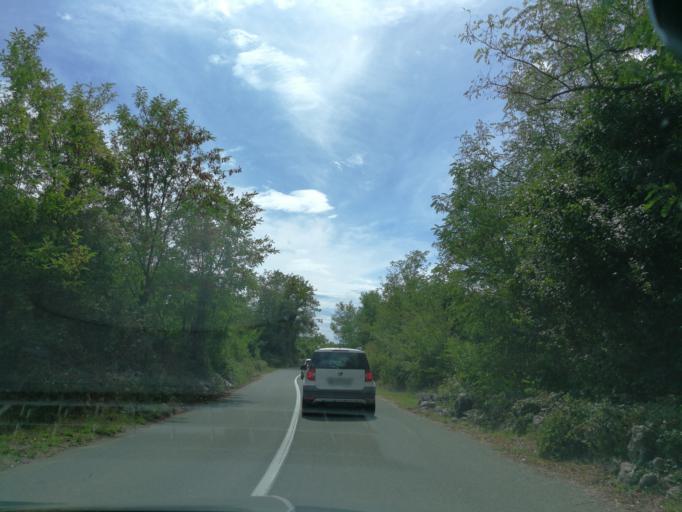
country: HR
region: Primorsko-Goranska
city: Punat
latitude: 45.1016
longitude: 14.6420
